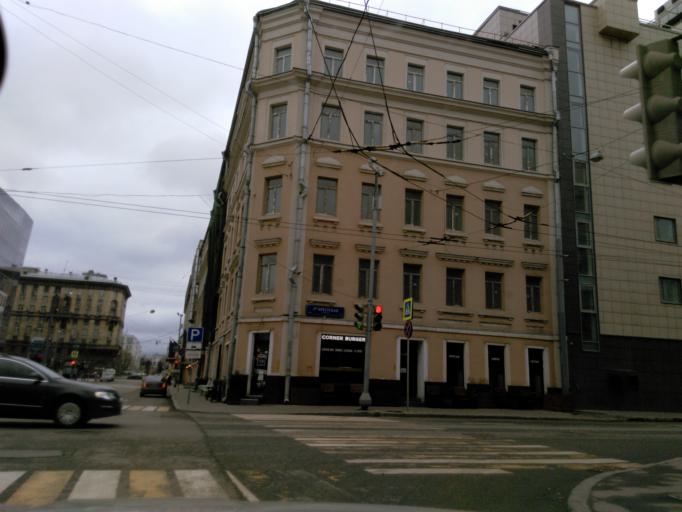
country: RU
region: Moskovskaya
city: Dorogomilovo
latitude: 55.7733
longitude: 37.5860
